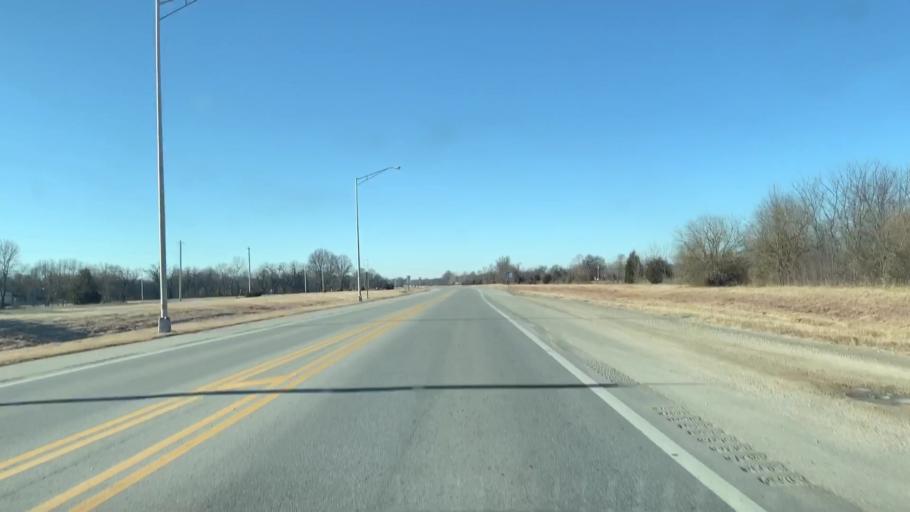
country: US
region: Kansas
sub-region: Cherokee County
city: Baxter Springs
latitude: 37.0743
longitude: -94.7179
